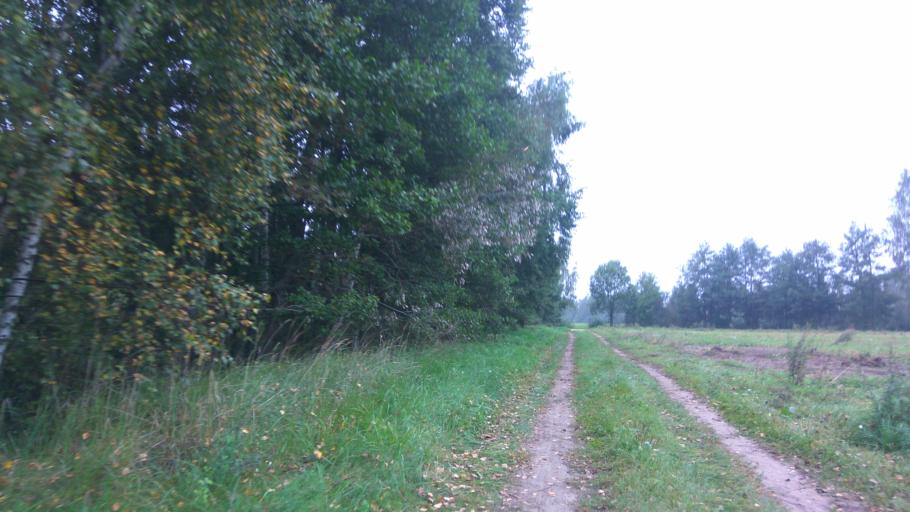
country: LV
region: Rucavas
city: Rucava
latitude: 56.1741
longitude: 21.1642
